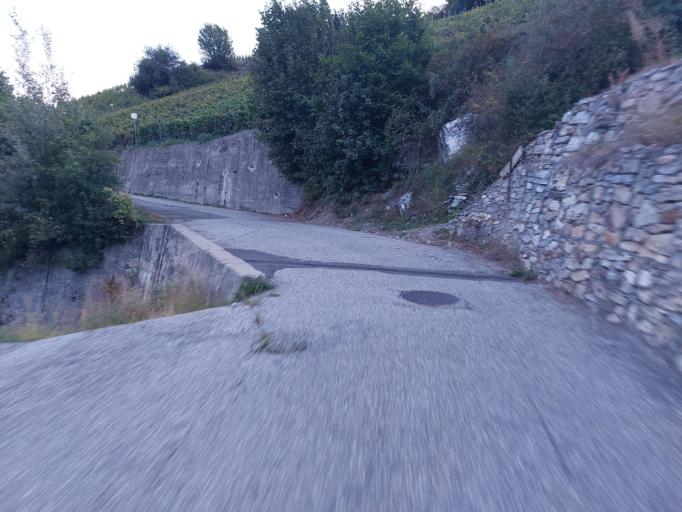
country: CH
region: Valais
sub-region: Conthey District
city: Conthey
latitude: 46.2482
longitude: 7.3073
